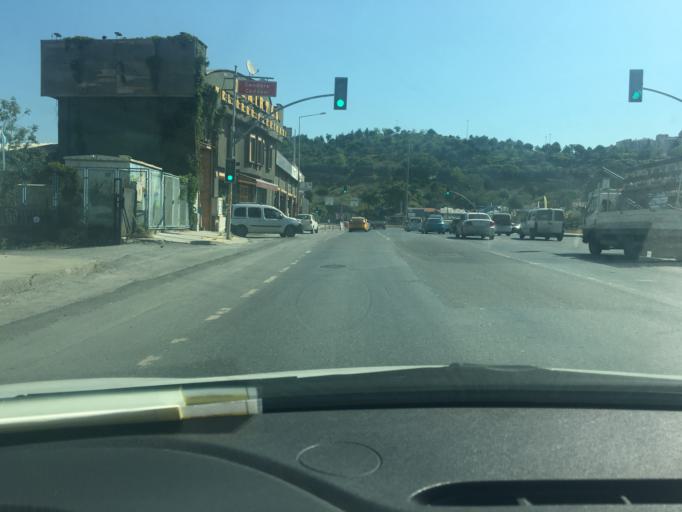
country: TR
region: Istanbul
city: Sisli
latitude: 41.0887
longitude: 28.9833
